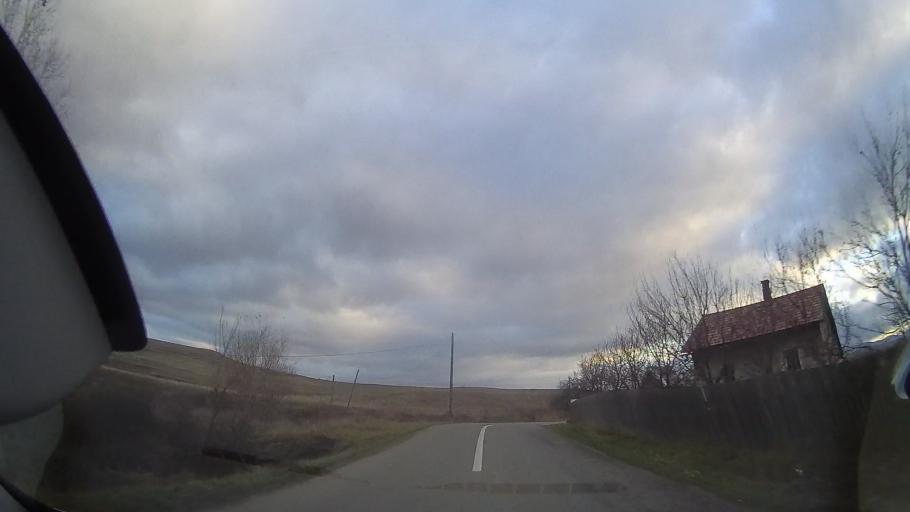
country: RO
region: Cluj
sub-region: Comuna Sancraiu
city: Sancraiu
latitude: 46.8189
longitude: 22.9949
